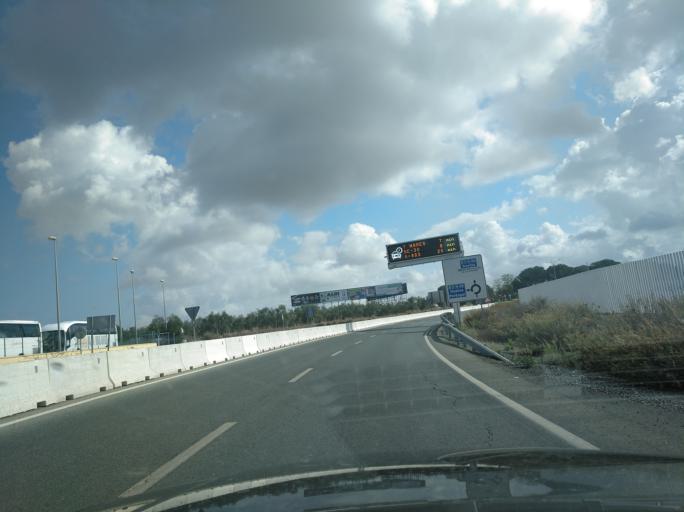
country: ES
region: Andalusia
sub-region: Provincia de Sevilla
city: Umbrete
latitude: 37.3621
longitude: -6.1443
